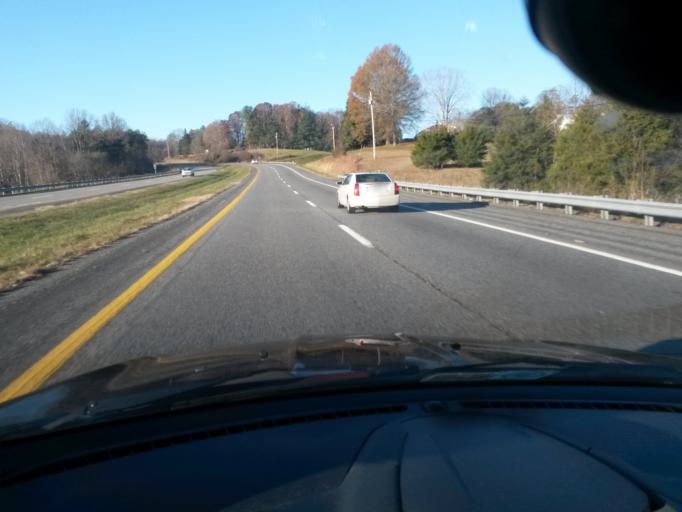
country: US
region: Virginia
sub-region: Henry County
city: Horse Pasture
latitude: 36.6088
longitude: -80.0452
